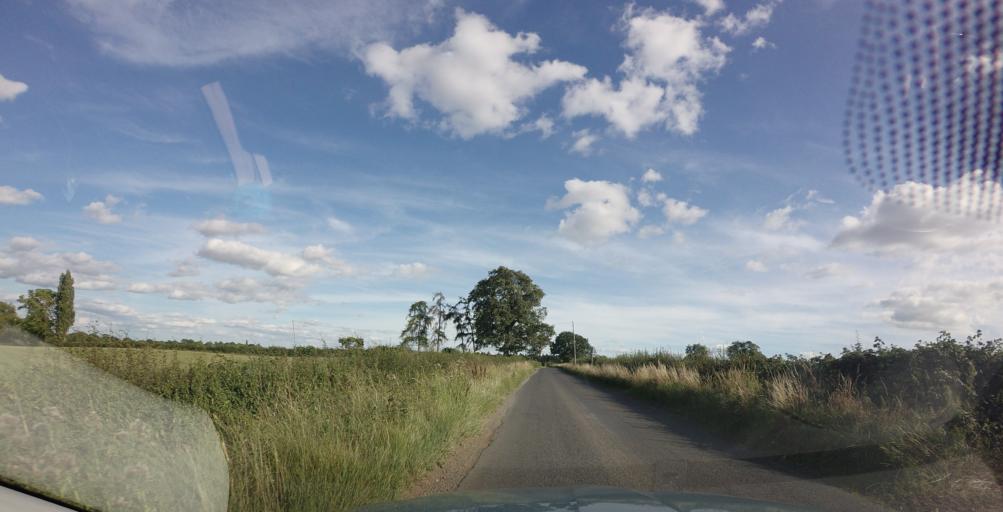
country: GB
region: England
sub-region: North Yorkshire
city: Ripon
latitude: 54.0974
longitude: -1.5105
